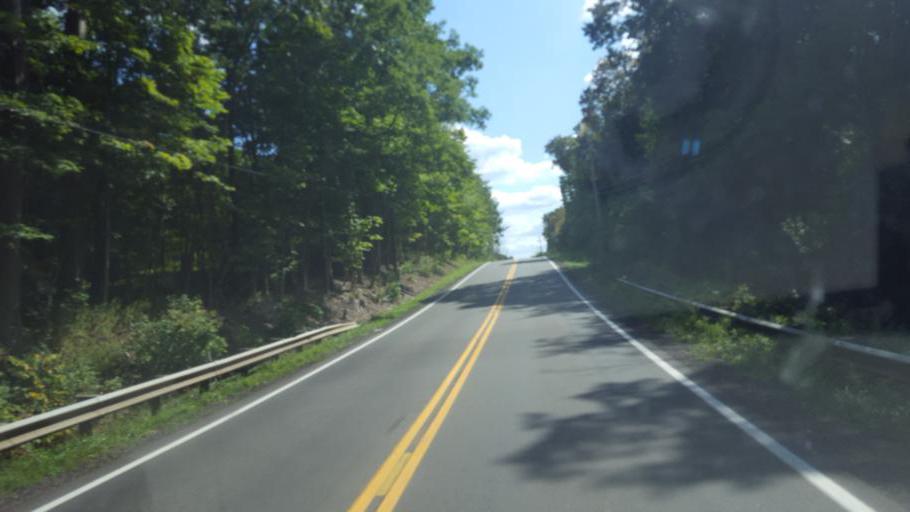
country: US
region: Ohio
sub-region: Ashland County
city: Ashland
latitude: 40.8801
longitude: -82.2114
